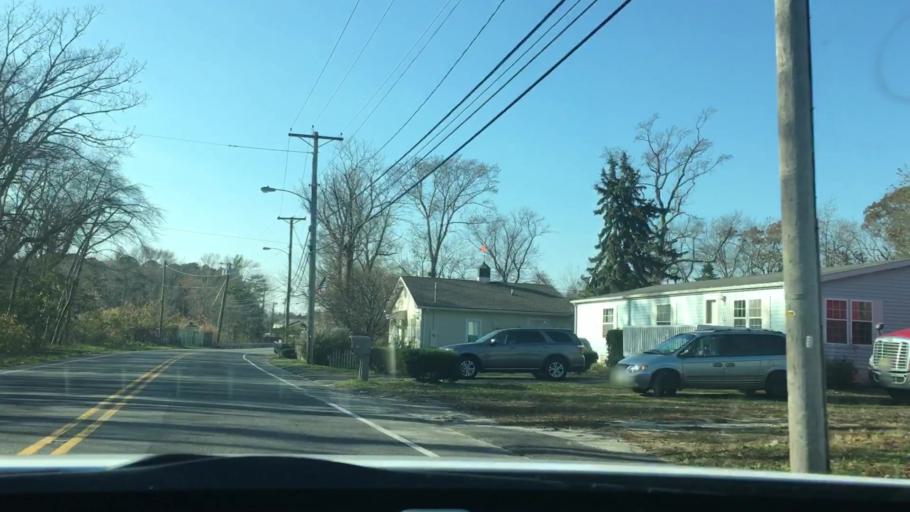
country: US
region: New Jersey
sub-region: Atlantic County
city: Absecon
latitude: 39.4137
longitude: -74.5053
